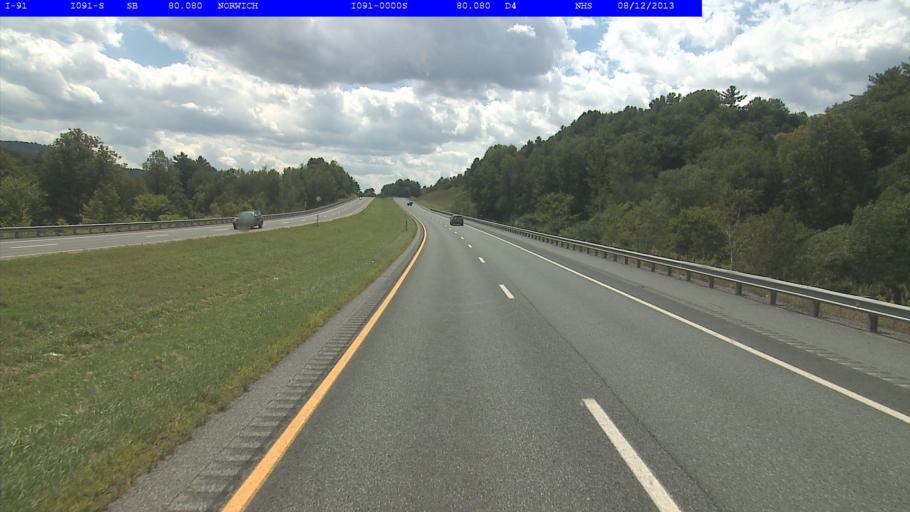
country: US
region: New Hampshire
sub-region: Grafton County
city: Hanover
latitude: 43.7587
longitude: -72.2348
